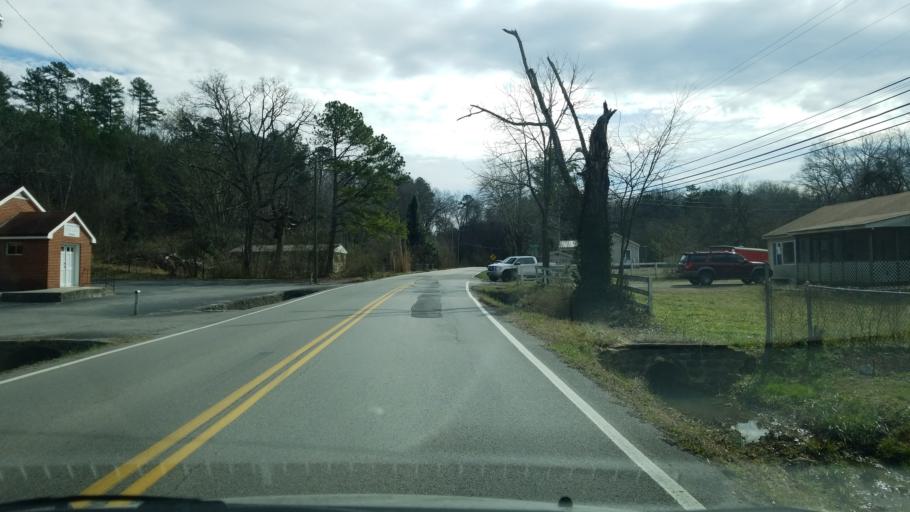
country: US
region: Tennessee
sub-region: Hamilton County
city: Harrison
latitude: 35.0662
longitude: -85.1156
